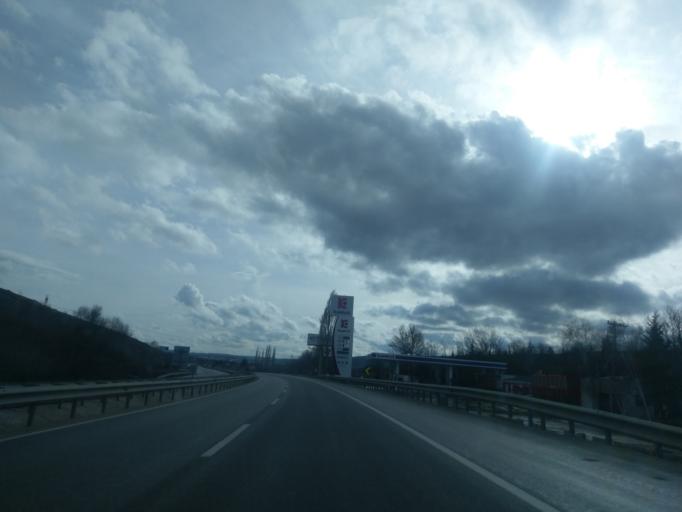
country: TR
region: Eskisehir
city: Inonu
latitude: 39.7033
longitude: 30.1542
